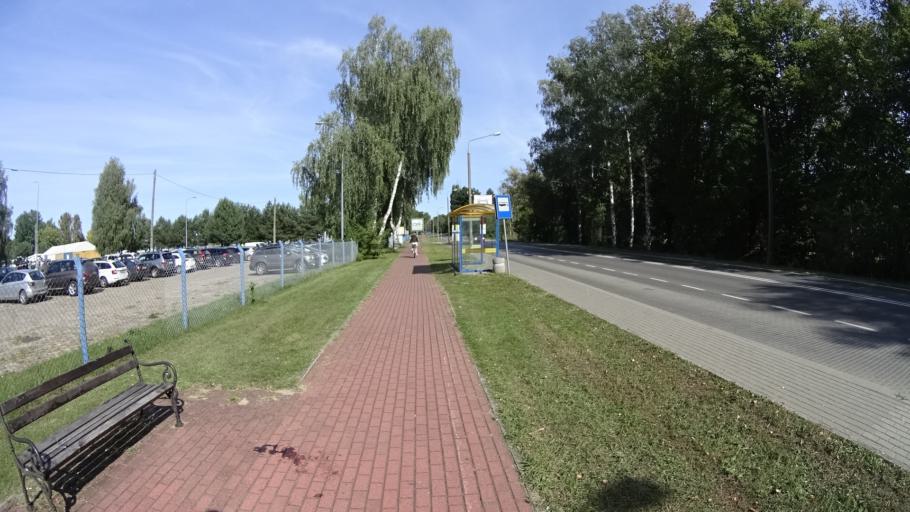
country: PL
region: Masovian Voivodeship
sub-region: Powiat legionowski
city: Nieporet
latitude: 52.4339
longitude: 21.0413
